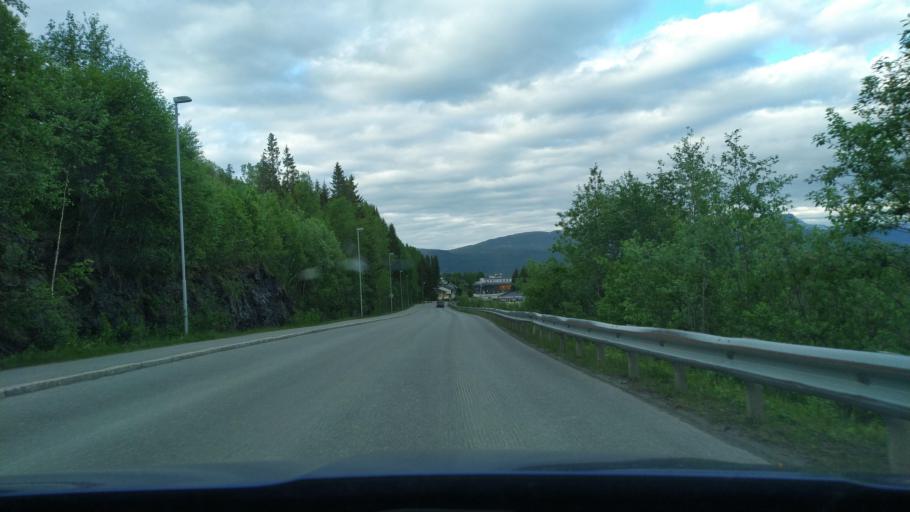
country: NO
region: Troms
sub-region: Malselv
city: Moen
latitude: 69.0633
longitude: 18.4983
